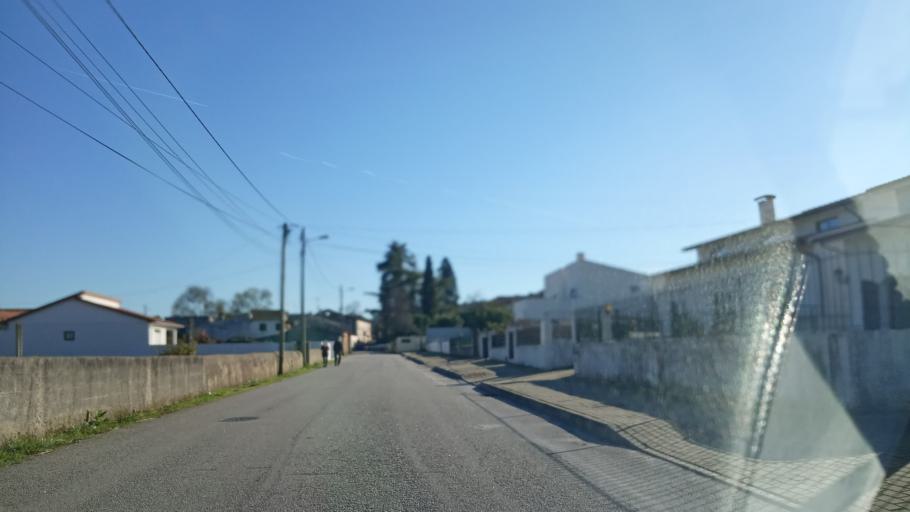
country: PT
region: Aveiro
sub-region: Anadia
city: Anadia
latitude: 40.4292
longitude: -8.4289
